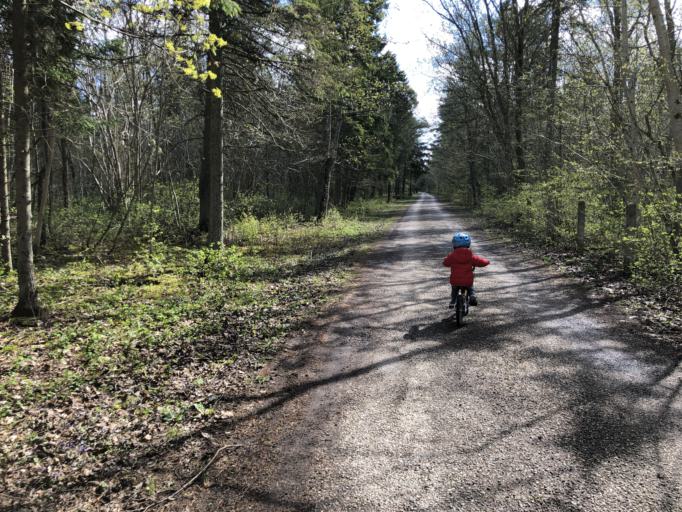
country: EE
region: Harju
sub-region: Harku vald
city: Tabasalu
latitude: 59.4382
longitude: 24.5327
